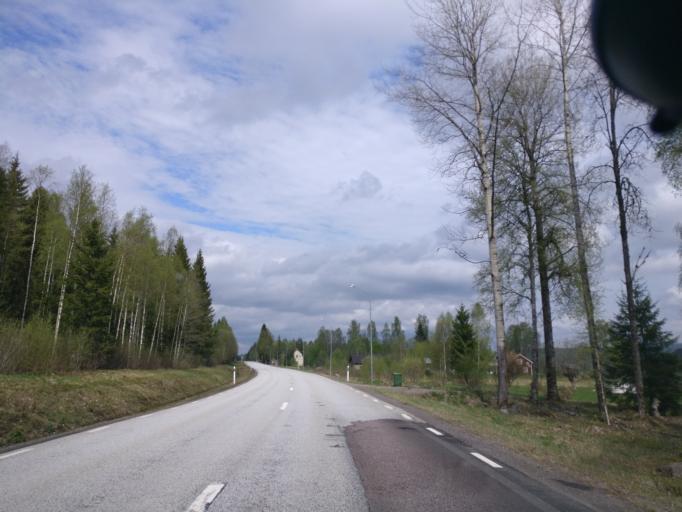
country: SE
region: Vaermland
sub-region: Hagfors Kommun
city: Ekshaerad
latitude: 60.1093
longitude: 13.5439
